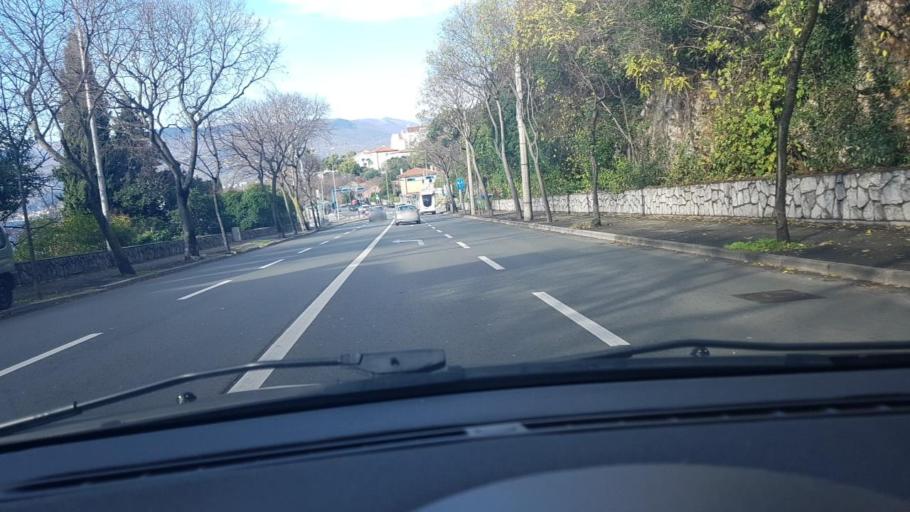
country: HR
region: Primorsko-Goranska
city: Rijeka
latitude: 45.3395
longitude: 14.3827
